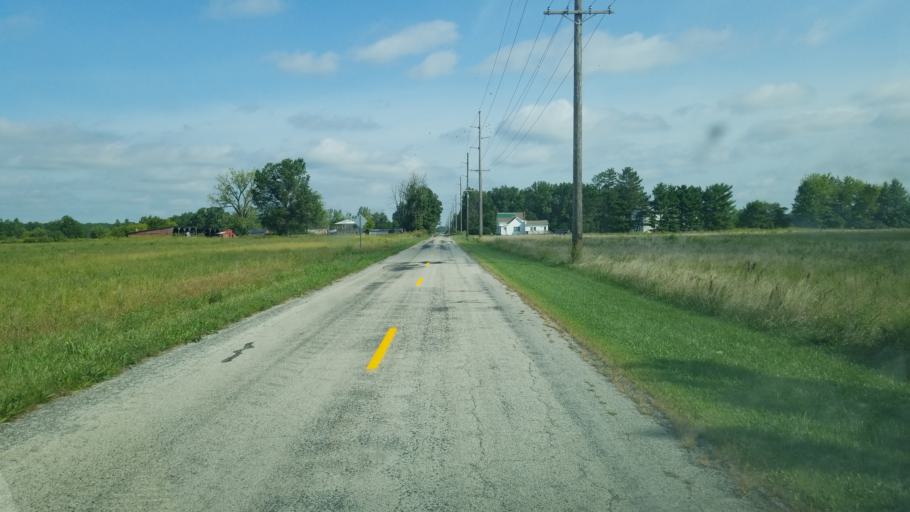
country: US
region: Ohio
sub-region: Wyandot County
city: Upper Sandusky
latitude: 40.6709
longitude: -83.3241
